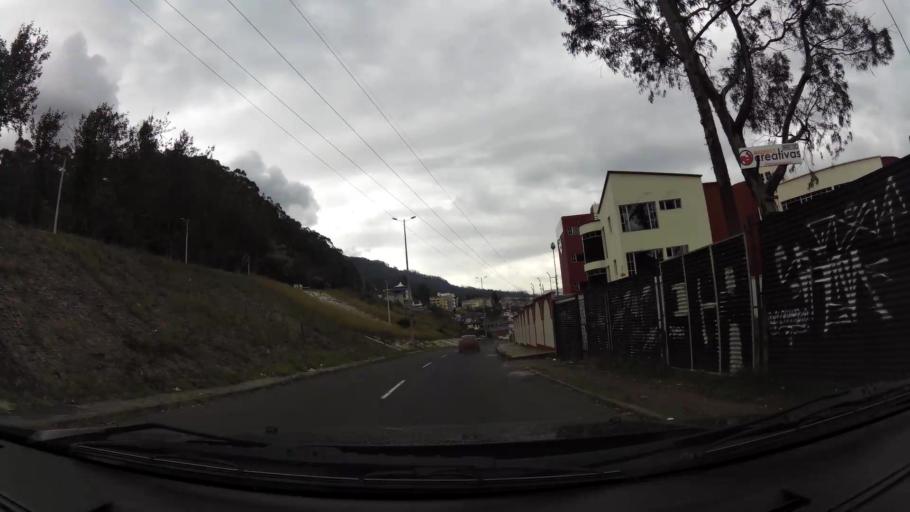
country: EC
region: Pichincha
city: Quito
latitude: -0.1969
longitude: -78.5123
